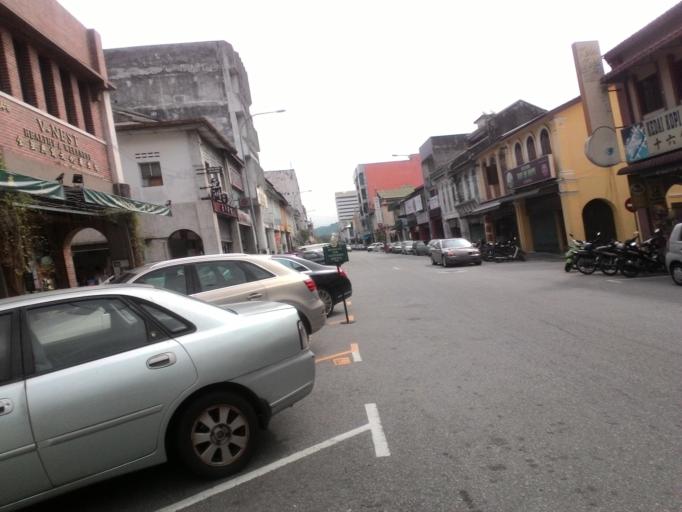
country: MY
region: Perak
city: Ipoh
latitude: 4.5934
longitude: 101.0771
